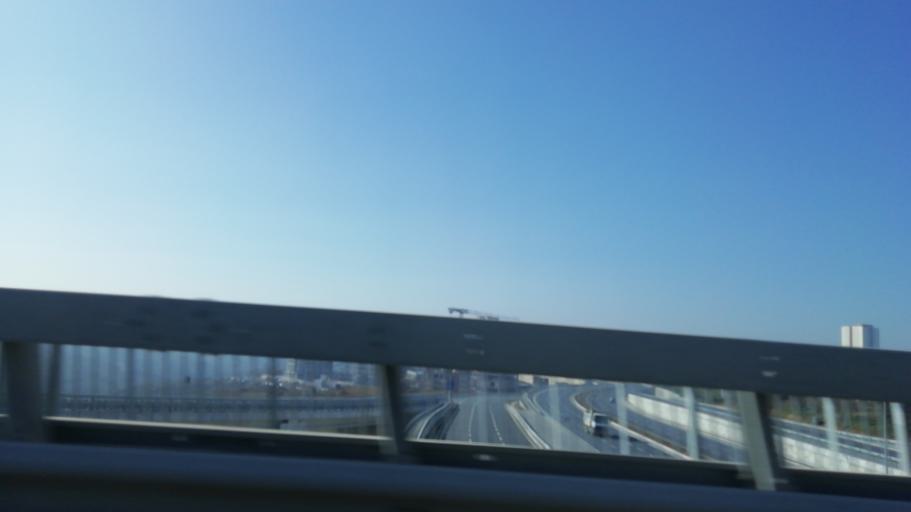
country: TR
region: Istanbul
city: Basaksehir
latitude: 41.1290
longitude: 28.7908
